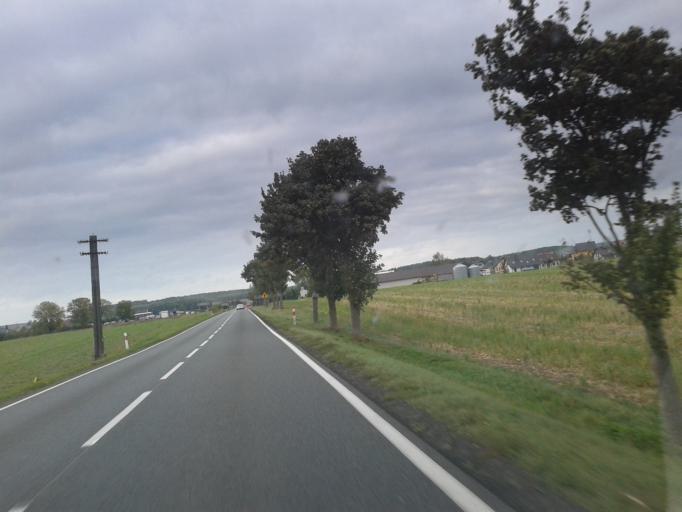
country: PL
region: Kujawsko-Pomorskie
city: Kamien Krajenski
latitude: 53.5258
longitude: 17.5116
